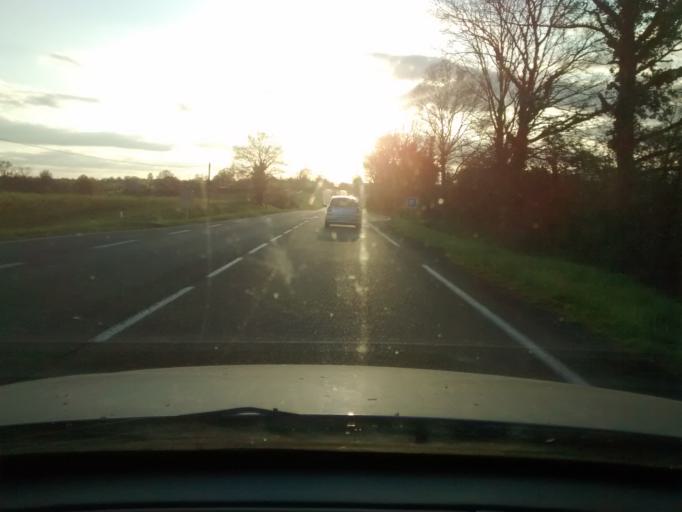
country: FR
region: Pays de la Loire
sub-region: Departement de la Mayenne
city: Sainte-Suzanne
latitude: 48.0340
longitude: -0.3743
